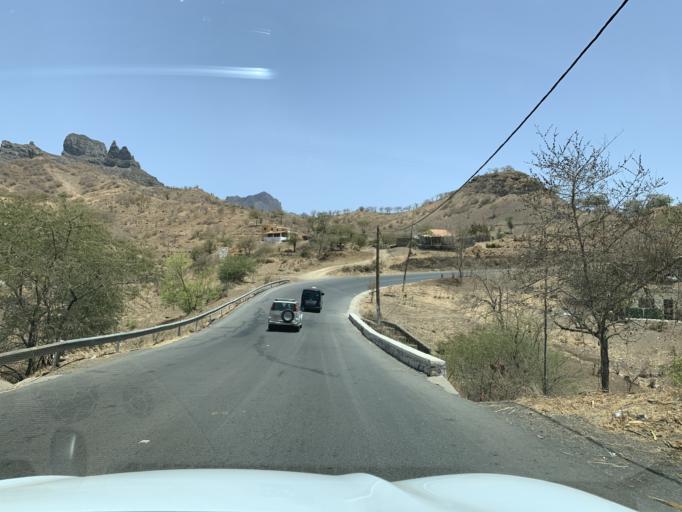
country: CV
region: Sao Lourenco dos Orgaos
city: Joao Teves
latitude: 15.0616
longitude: -23.5746
